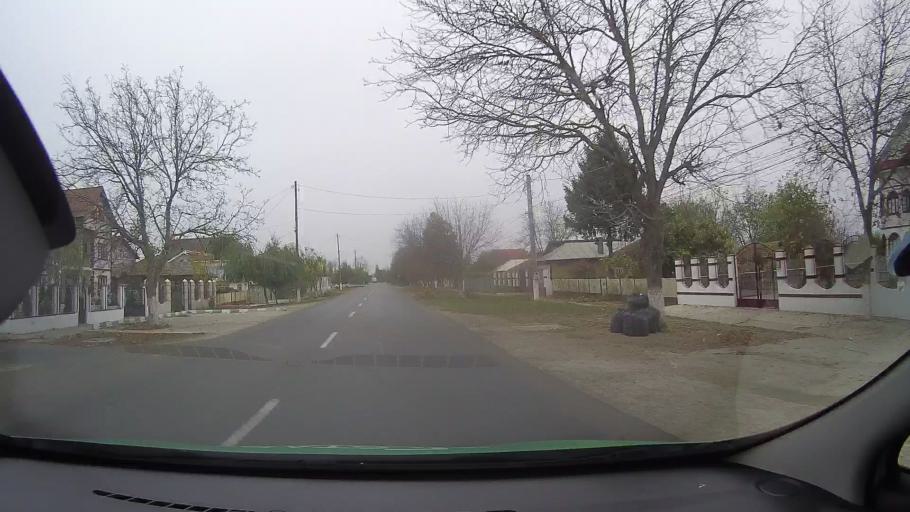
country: RO
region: Ialomita
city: Tandarei
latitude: 44.6510
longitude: 27.6550
